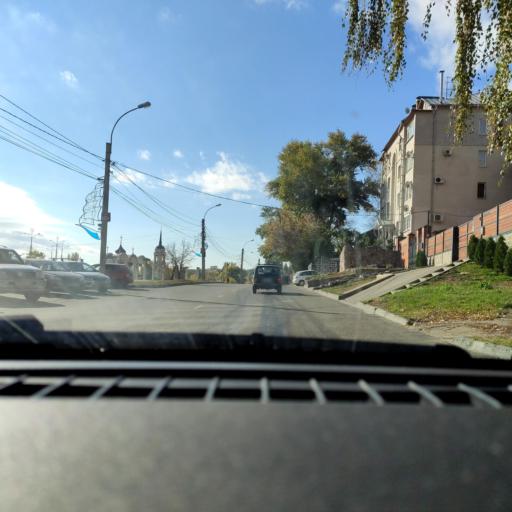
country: RU
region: Voronezj
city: Voronezh
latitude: 51.6592
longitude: 39.2154
